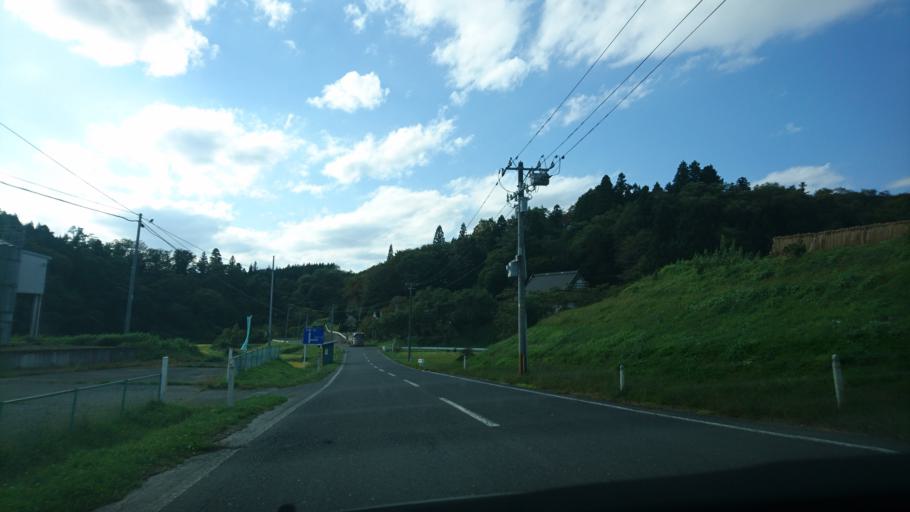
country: JP
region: Iwate
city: Ichinoseki
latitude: 38.8721
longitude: 141.3475
